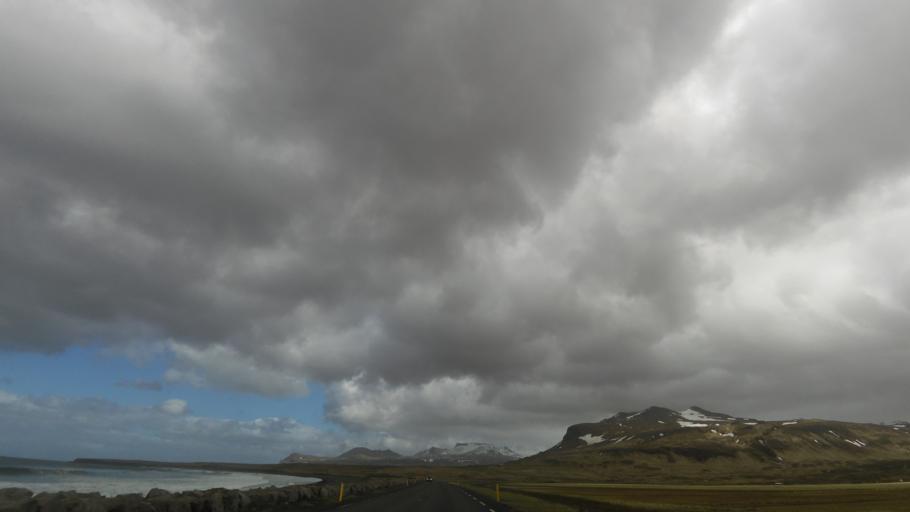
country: IS
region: West
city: Olafsvik
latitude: 64.8903
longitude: -23.6303
